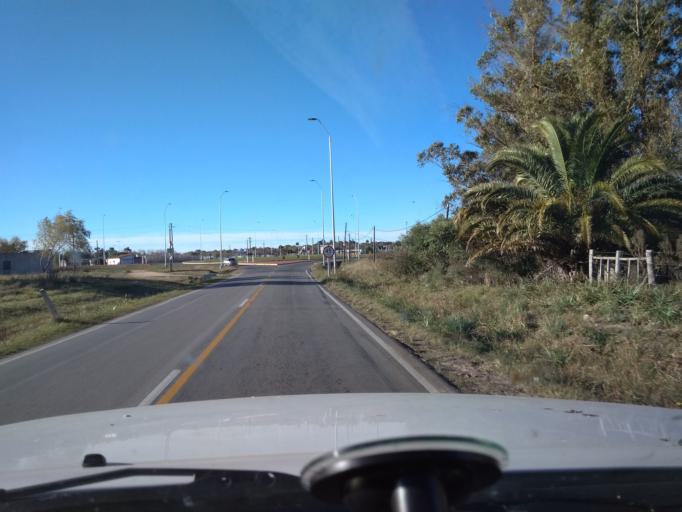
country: UY
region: Canelones
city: Santa Rosa
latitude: -34.5061
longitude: -56.0499
